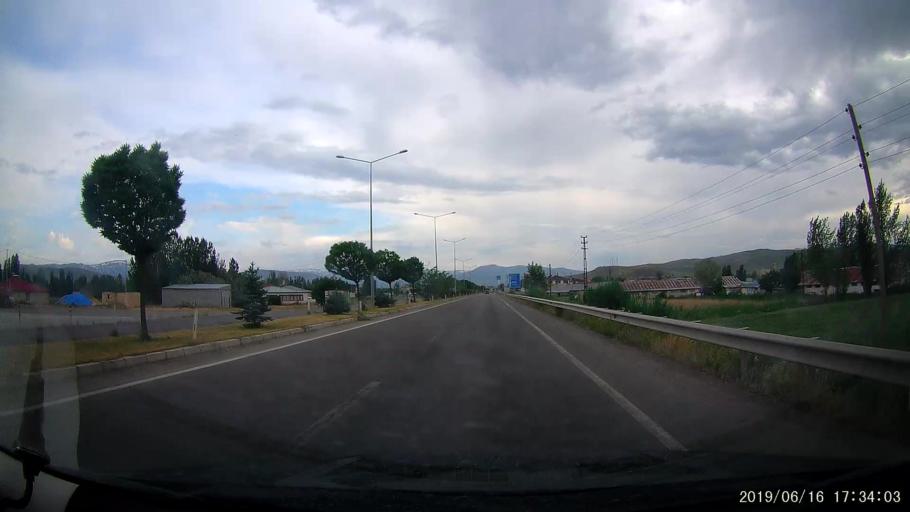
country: TR
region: Erzincan
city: Tercan
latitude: 39.7450
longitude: 40.2726
